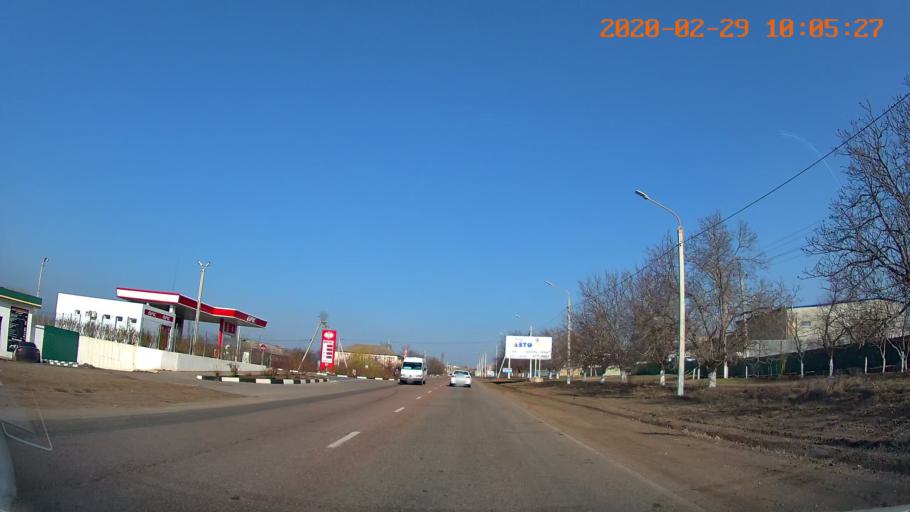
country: MD
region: Telenesti
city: Tiraspolul Nou
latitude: 46.8072
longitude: 29.6713
